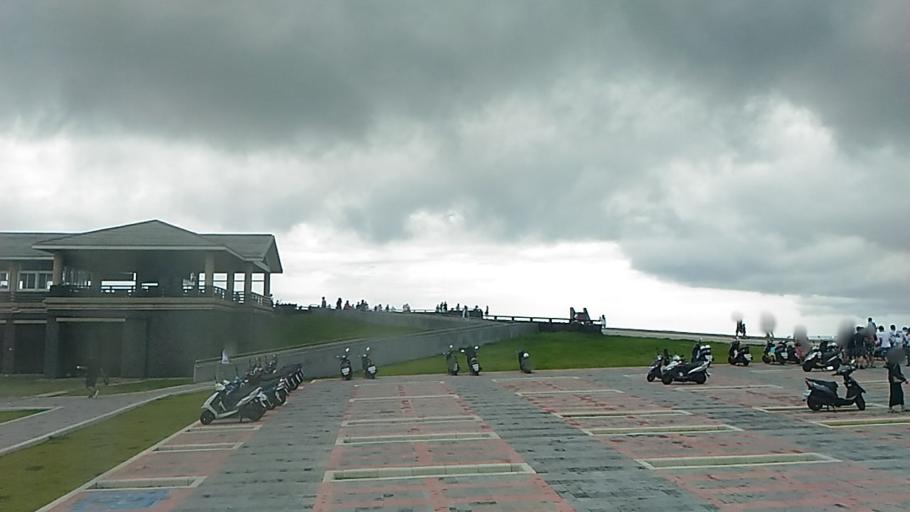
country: TW
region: Taiwan
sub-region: Penghu
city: Ma-kung
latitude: 23.2188
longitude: 119.4460
